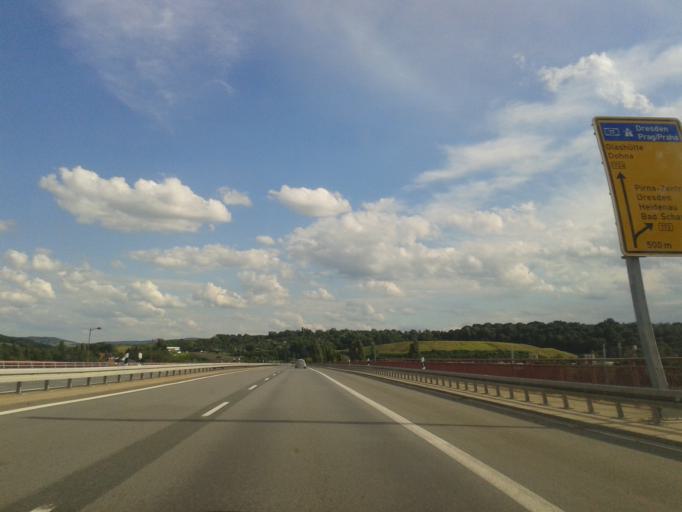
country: DE
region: Saxony
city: Pirna
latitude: 50.9623
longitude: 13.9166
